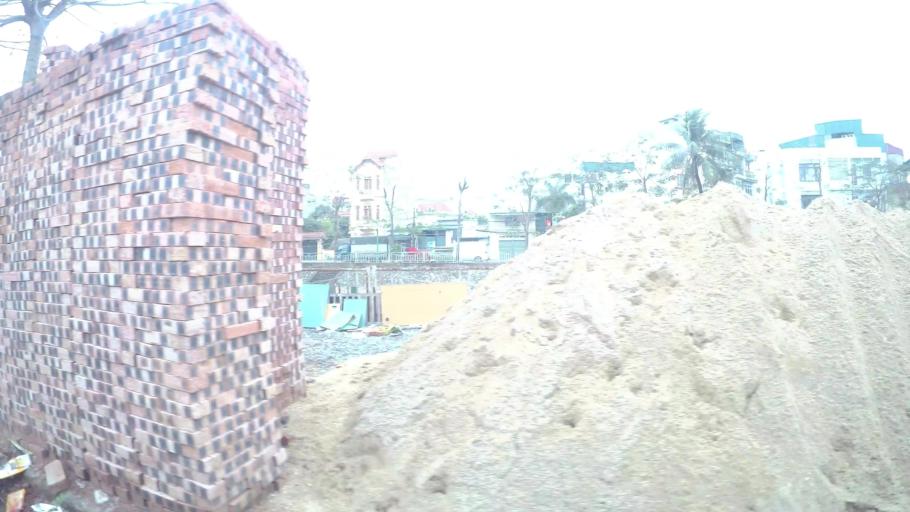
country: VN
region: Ha Noi
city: Van Dien
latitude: 20.9747
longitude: 105.8505
